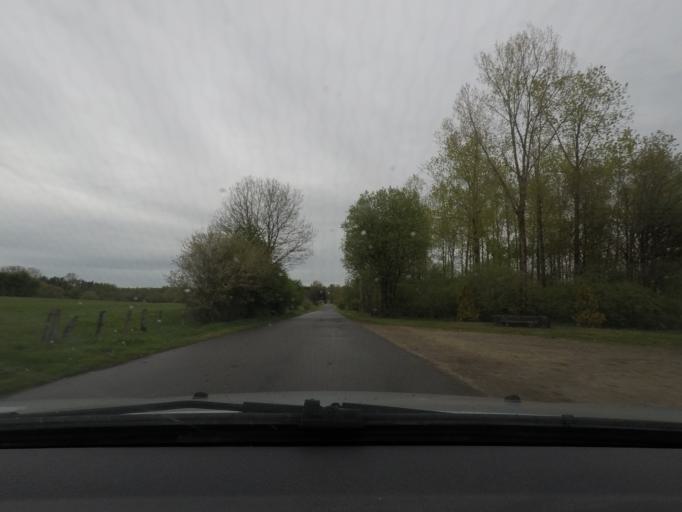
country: BE
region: Wallonia
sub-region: Province du Luxembourg
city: Etalle
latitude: 49.6829
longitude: 5.5643
